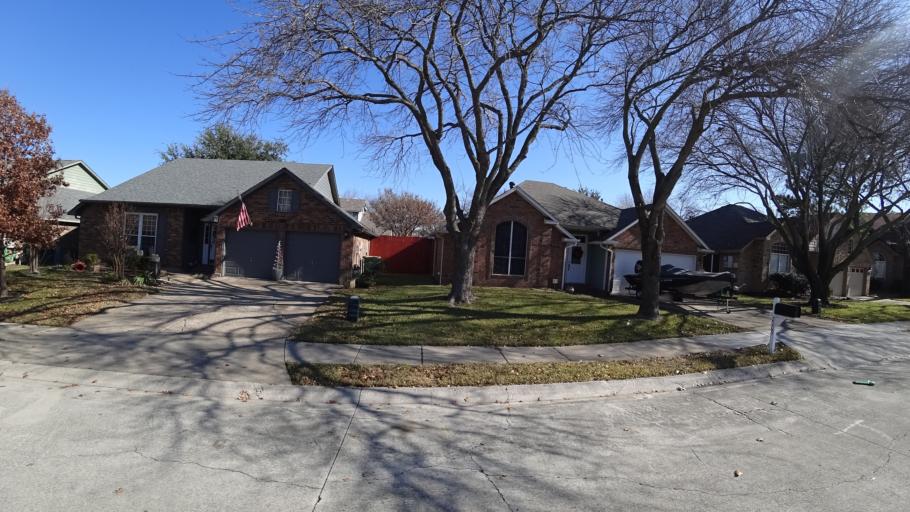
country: US
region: Texas
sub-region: Denton County
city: Lewisville
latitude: 33.0161
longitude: -97.0265
